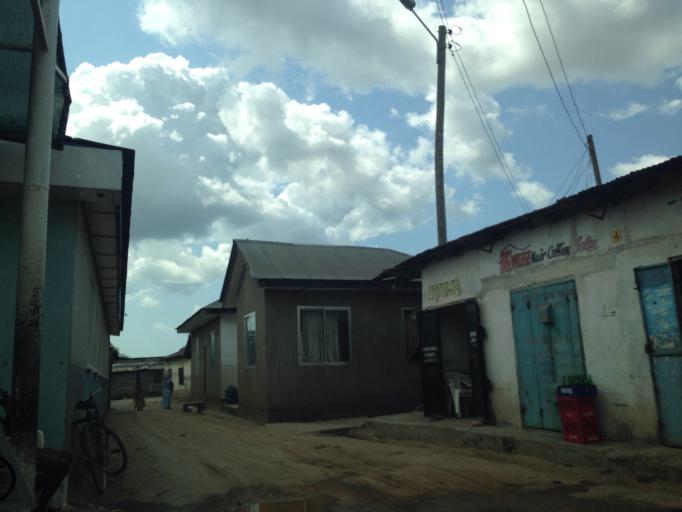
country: TZ
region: Dar es Salaam
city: Dar es Salaam
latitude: -6.8368
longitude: 39.2729
